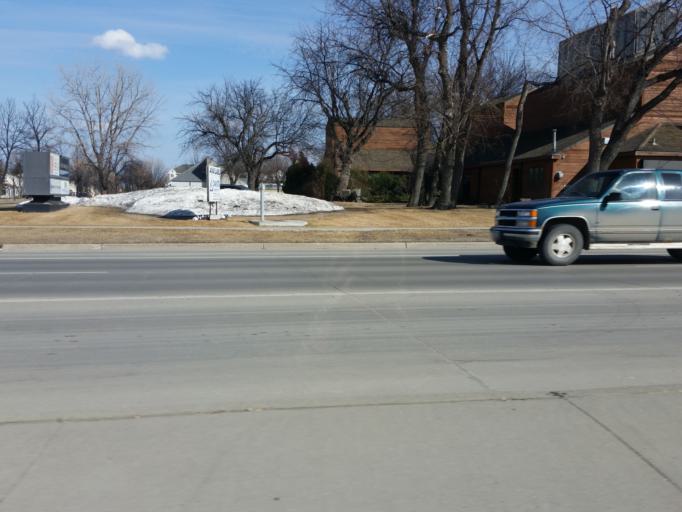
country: US
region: North Dakota
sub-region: Grand Forks County
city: Grand Forks
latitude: 47.8943
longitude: -97.0668
